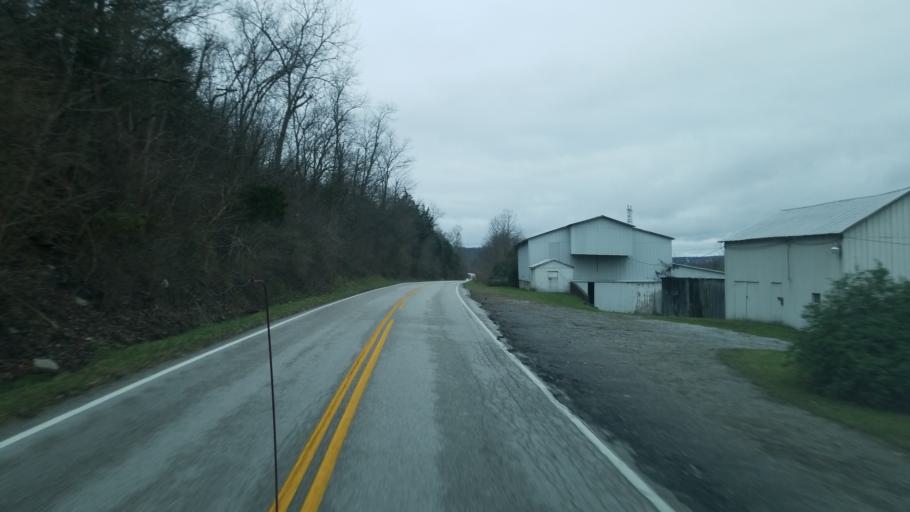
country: US
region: Kentucky
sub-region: Bracken County
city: Brooksville
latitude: 38.7877
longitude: -84.1603
